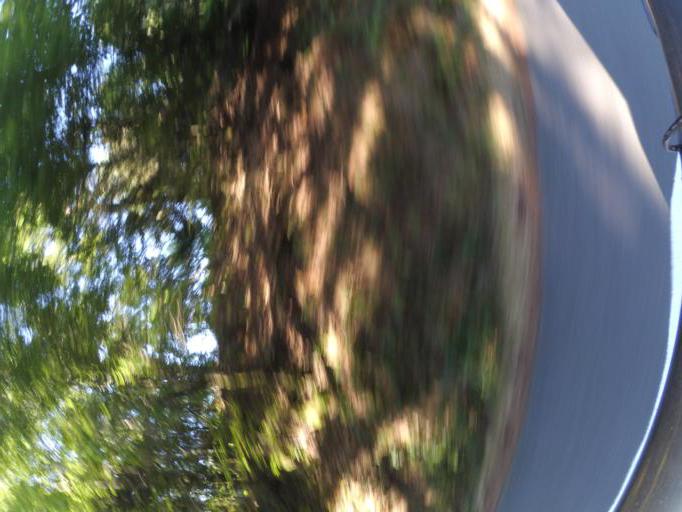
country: FR
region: Limousin
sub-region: Departement de la Correze
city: Bugeat
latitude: 45.7593
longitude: 1.9254
